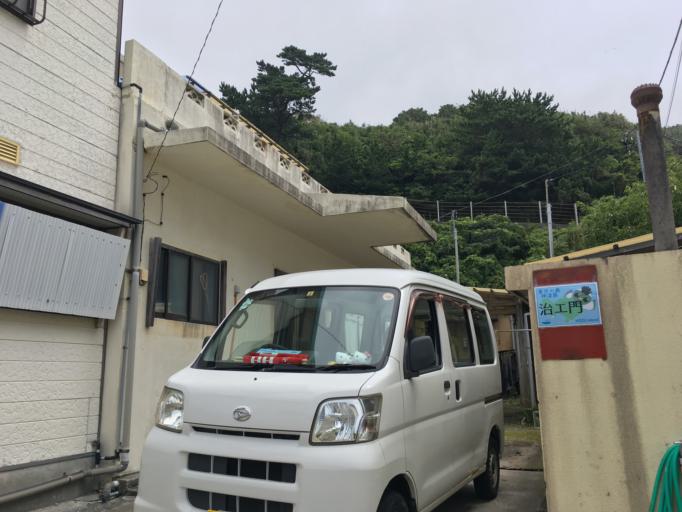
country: JP
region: Shizuoka
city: Shimoda
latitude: 34.2074
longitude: 139.1373
